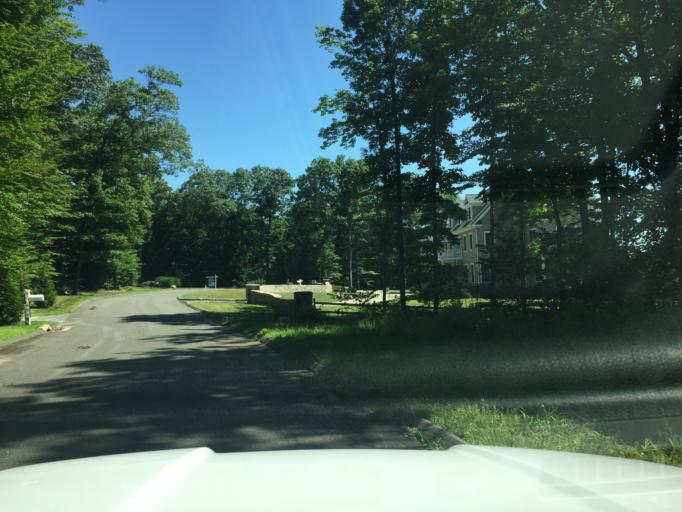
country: US
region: Connecticut
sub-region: Fairfield County
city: Westport
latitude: 41.2171
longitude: -73.3536
